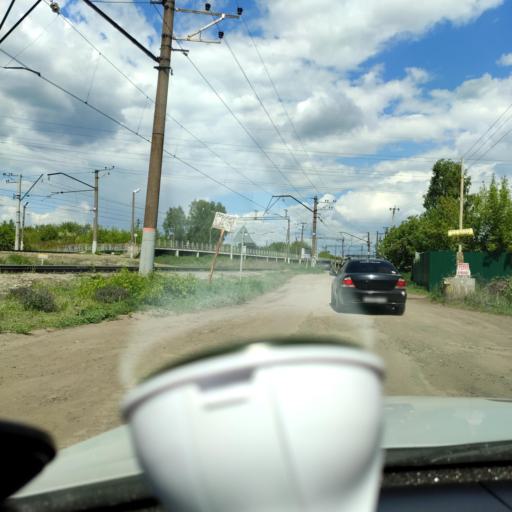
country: RU
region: Samara
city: Petra-Dubrava
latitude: 53.2691
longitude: 50.3173
